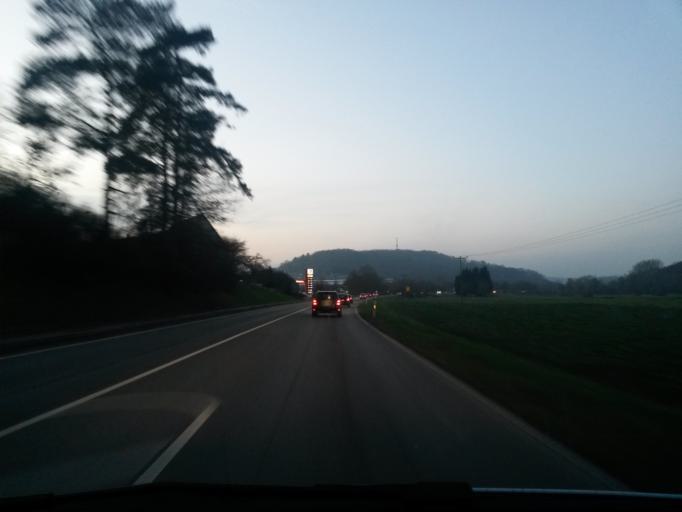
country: DE
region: Baden-Wuerttemberg
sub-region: Regierungsbezirk Stuttgart
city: Aidlingen
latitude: 48.7143
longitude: 8.9028
